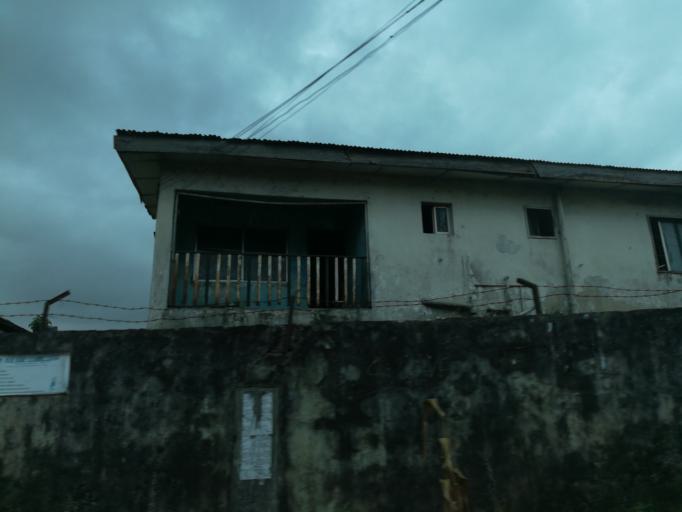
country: NG
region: Rivers
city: Port Harcourt
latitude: 4.8370
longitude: 7.0279
